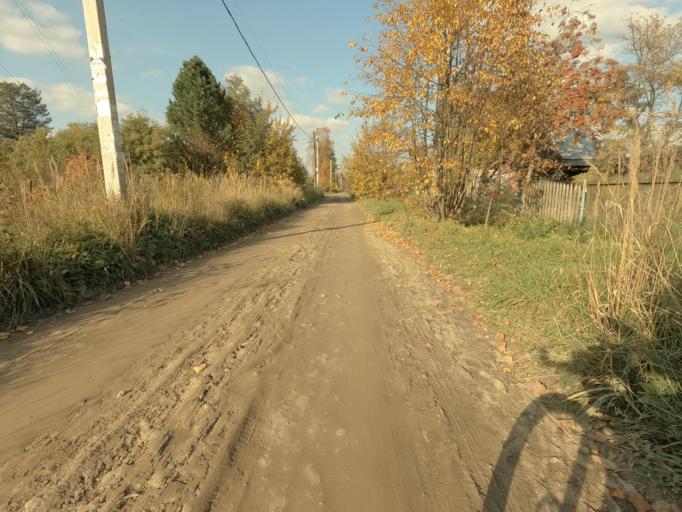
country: RU
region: Leningrad
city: Mga
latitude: 59.7629
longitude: 31.1169
